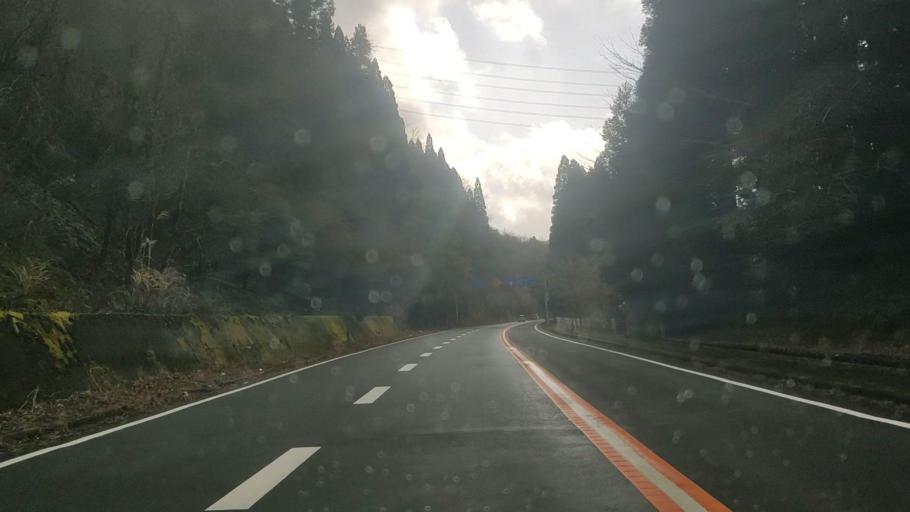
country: JP
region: Kumamoto
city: Hitoyoshi
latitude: 32.1113
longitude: 130.8055
